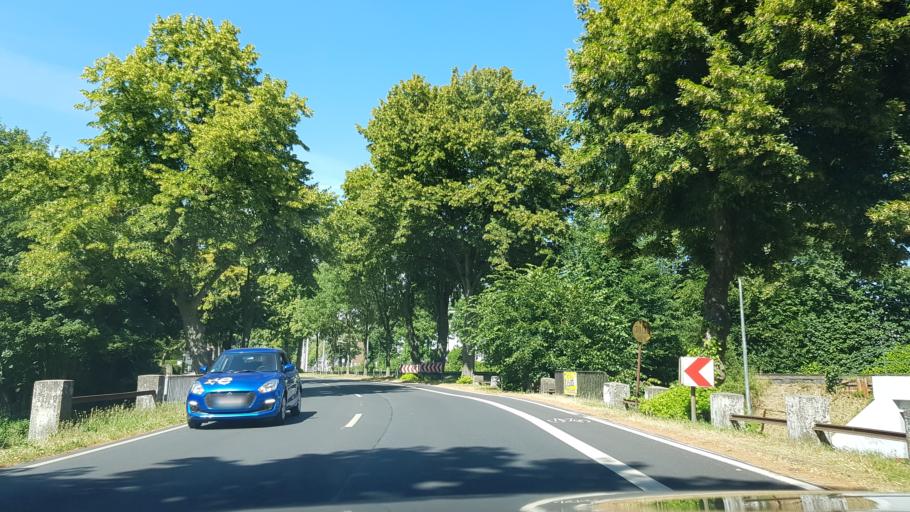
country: DE
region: North Rhine-Westphalia
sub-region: Regierungsbezirk Dusseldorf
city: Meerbusch
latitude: 51.2988
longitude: 6.7385
